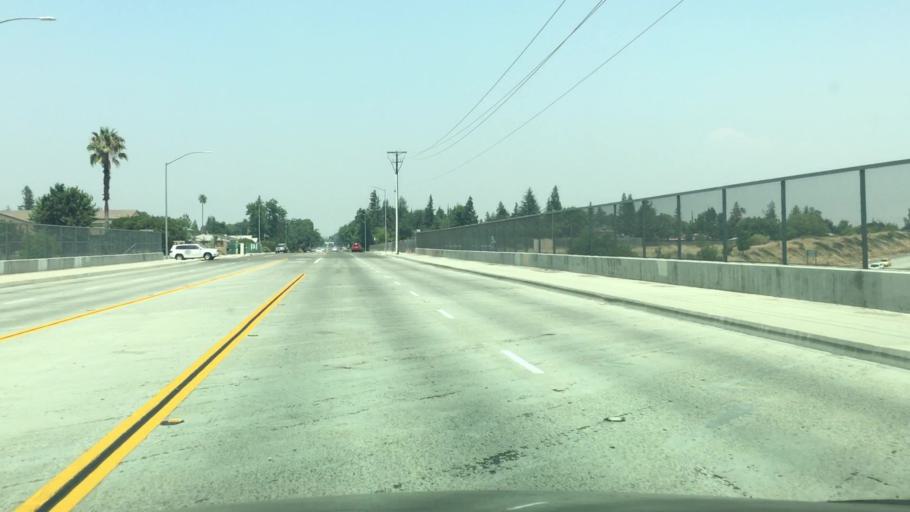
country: US
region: California
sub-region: Fresno County
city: Clovis
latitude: 36.8260
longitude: -119.7134
